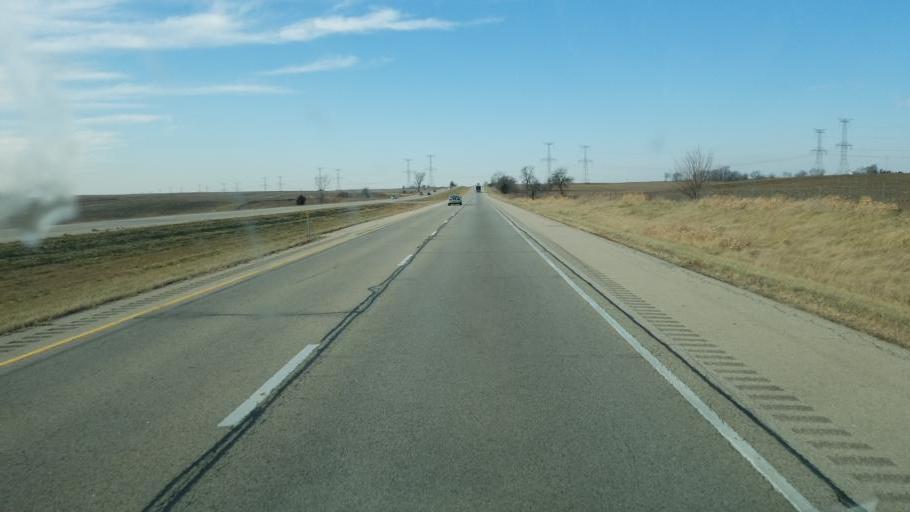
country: US
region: Illinois
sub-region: Tazewell County
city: Morton
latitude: 40.6225
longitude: -89.3775
